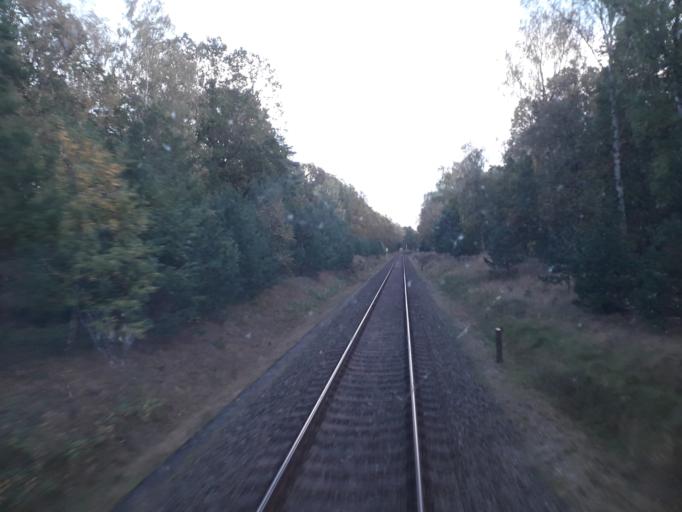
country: DE
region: Brandenburg
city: Walsleben
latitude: 53.0155
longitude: 12.6011
